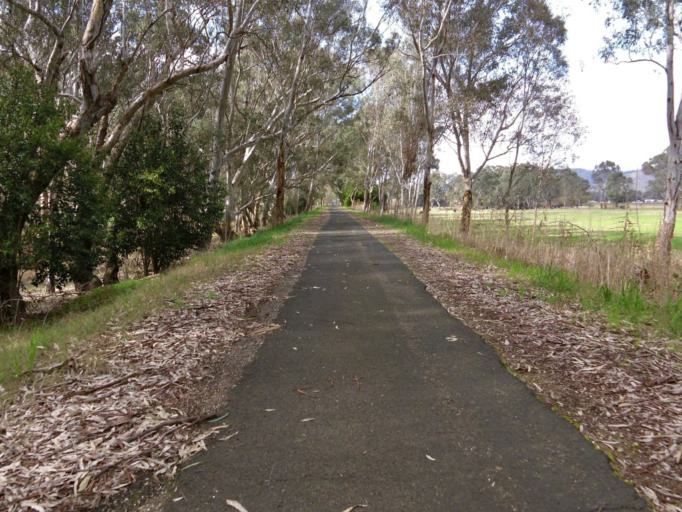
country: AU
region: Victoria
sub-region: Alpine
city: Mount Beauty
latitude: -36.5834
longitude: 146.7529
